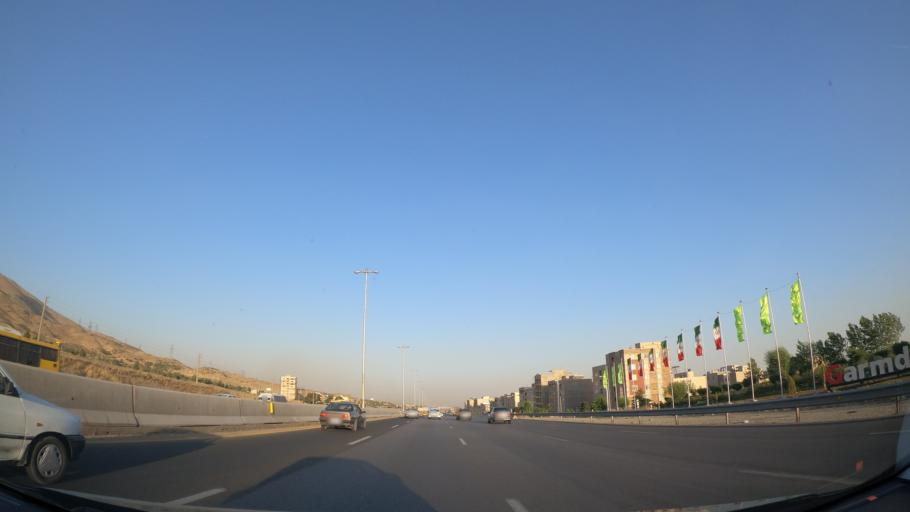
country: IR
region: Tehran
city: Shahr-e Qods
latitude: 35.7598
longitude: 51.0656
